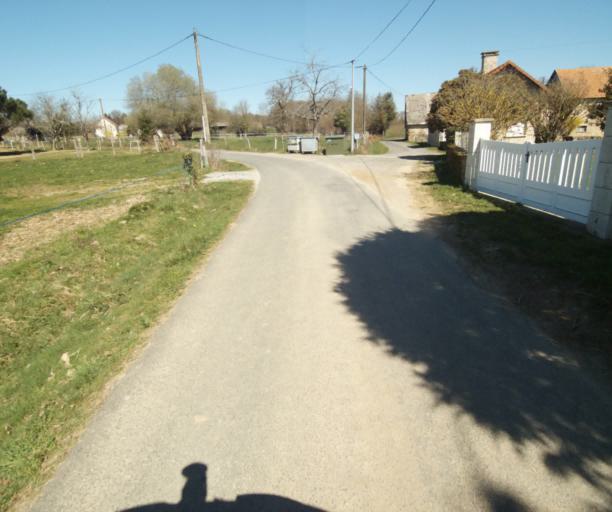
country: FR
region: Limousin
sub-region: Departement de la Correze
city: Saint-Mexant
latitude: 45.3129
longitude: 1.6578
